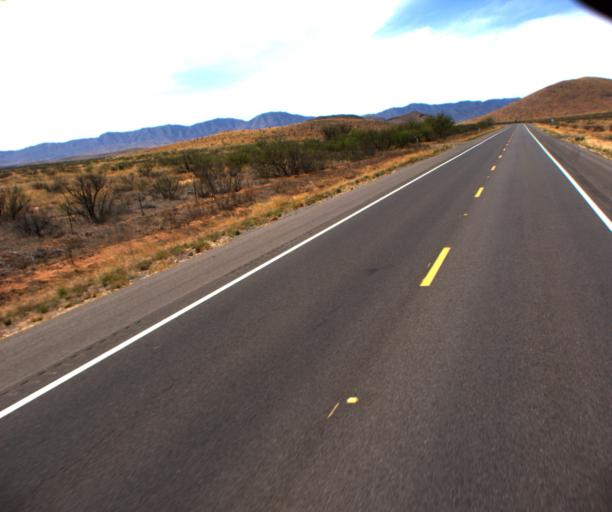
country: US
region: Arizona
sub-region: Cochise County
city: Tombstone
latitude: 31.9054
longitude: -109.7787
